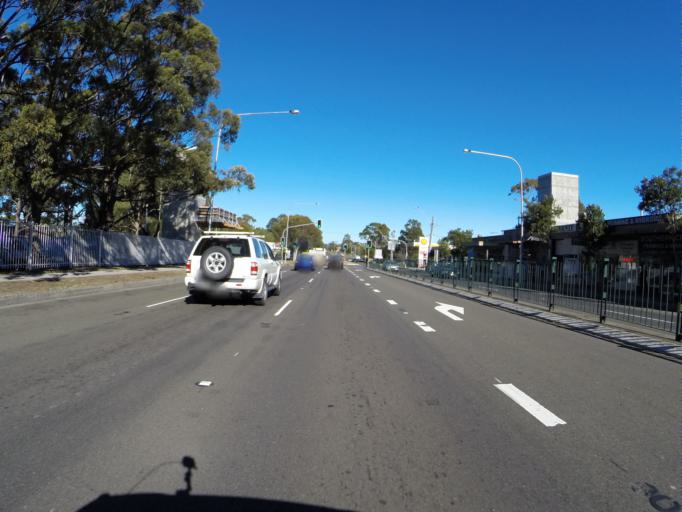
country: AU
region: New South Wales
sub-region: Sutherland Shire
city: Heathcote
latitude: -34.0875
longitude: 151.0080
